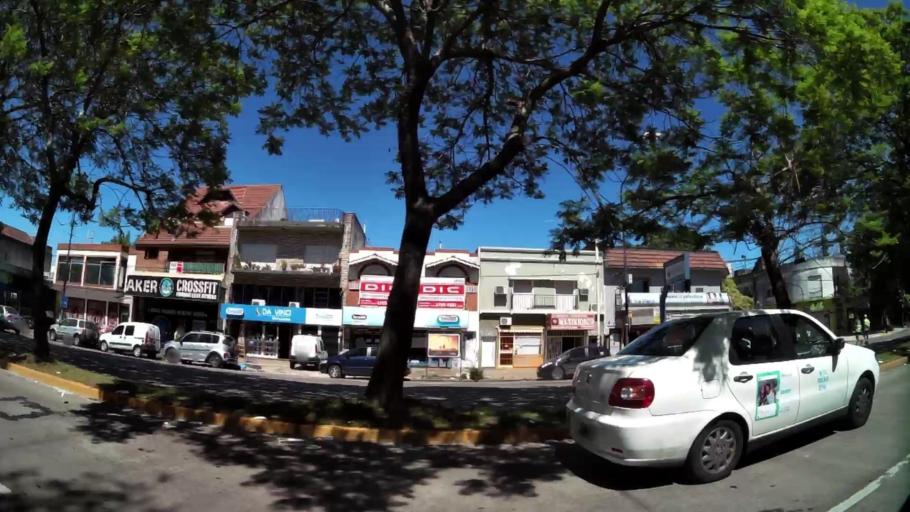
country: AR
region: Buenos Aires
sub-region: Partido de Vicente Lopez
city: Olivos
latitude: -34.4991
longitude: -58.4969
